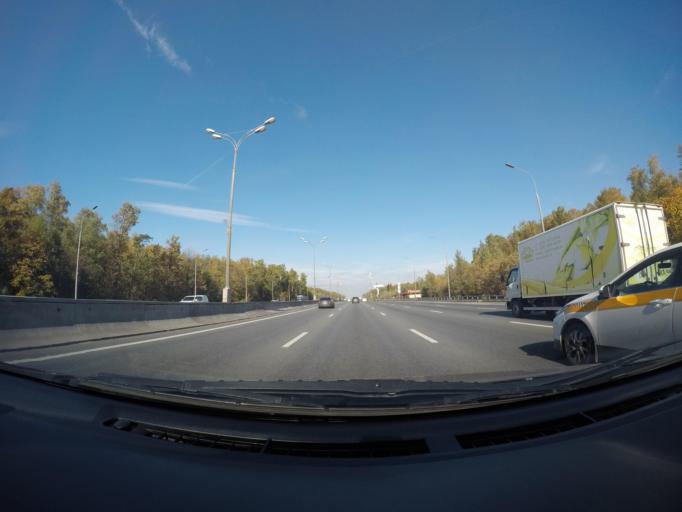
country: RU
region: Moscow
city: Ivanovskoye
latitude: 55.7913
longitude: 37.8413
